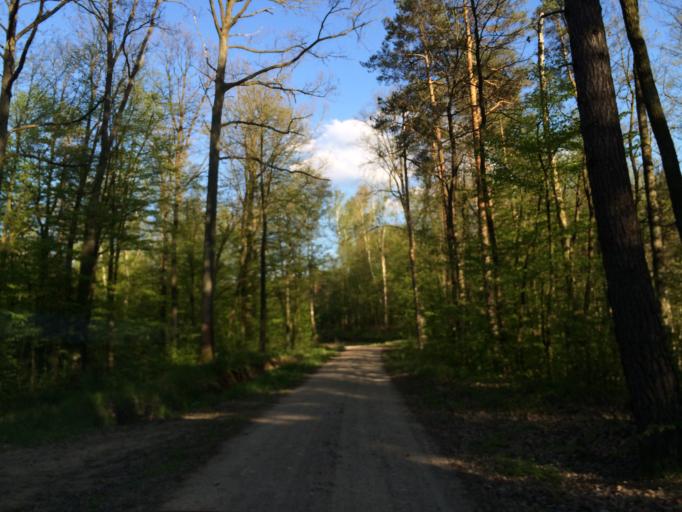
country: PL
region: Warmian-Masurian Voivodeship
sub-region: Powiat dzialdowski
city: Lidzbark
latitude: 53.2690
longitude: 19.7349
